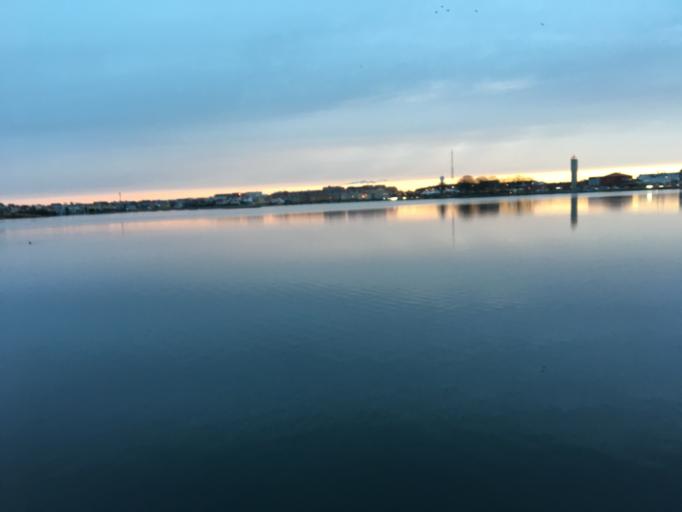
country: SE
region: Blekinge
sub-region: Karlskrona Kommun
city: Karlskrona
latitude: 56.1648
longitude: 15.5744
